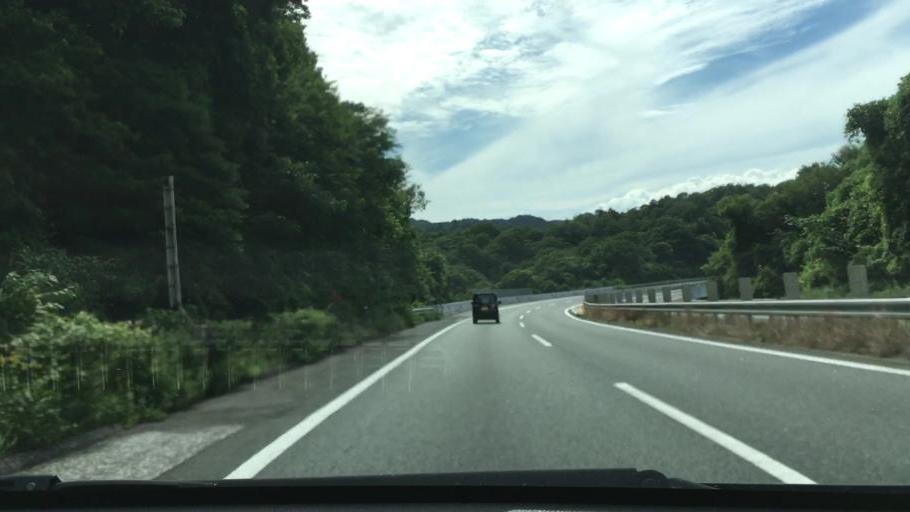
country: JP
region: Yamaguchi
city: Ogori-shimogo
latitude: 34.1268
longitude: 131.3861
